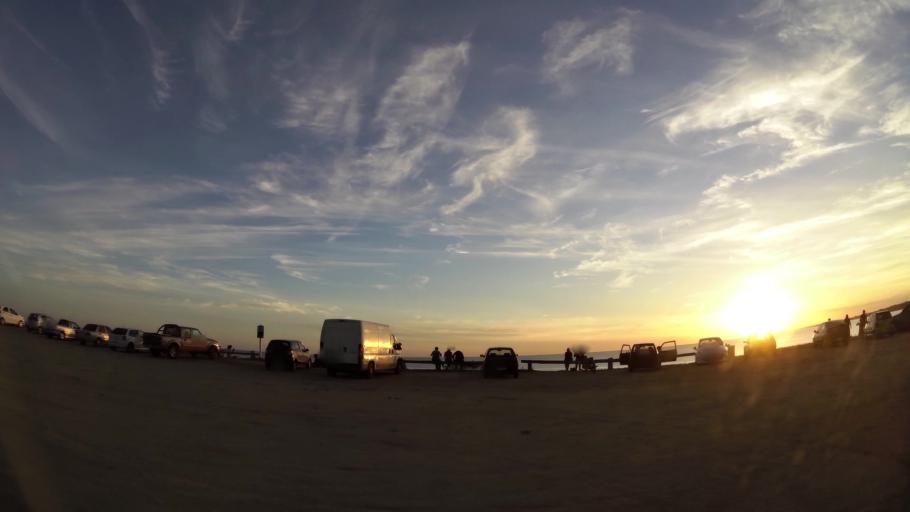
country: UY
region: Canelones
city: Atlantida
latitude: -34.7731
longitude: -55.7679
